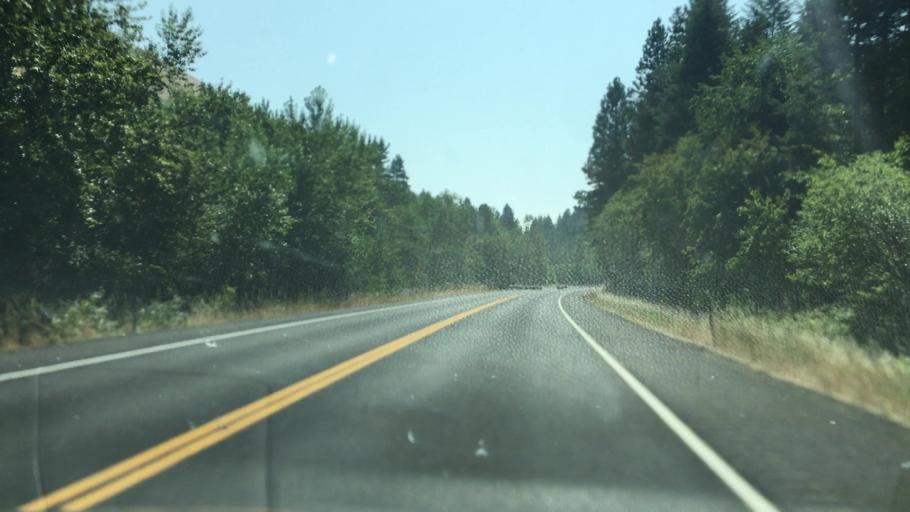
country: US
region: Idaho
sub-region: Nez Perce County
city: Lapwai
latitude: 46.3588
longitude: -116.6310
